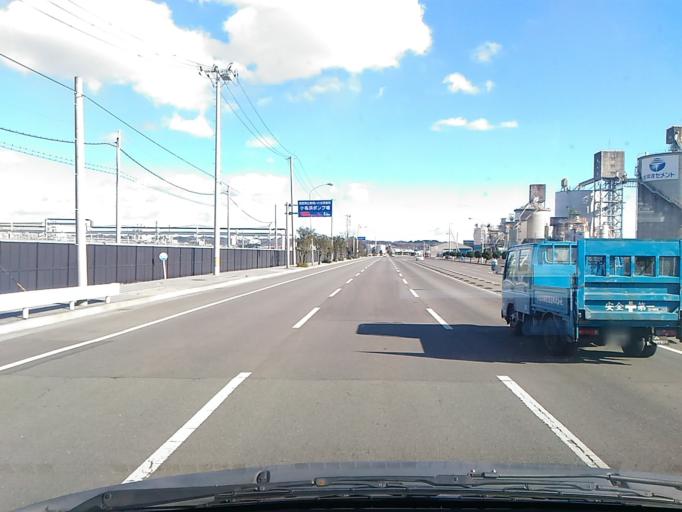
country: JP
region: Fukushima
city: Iwaki
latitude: 36.9418
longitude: 140.8891
